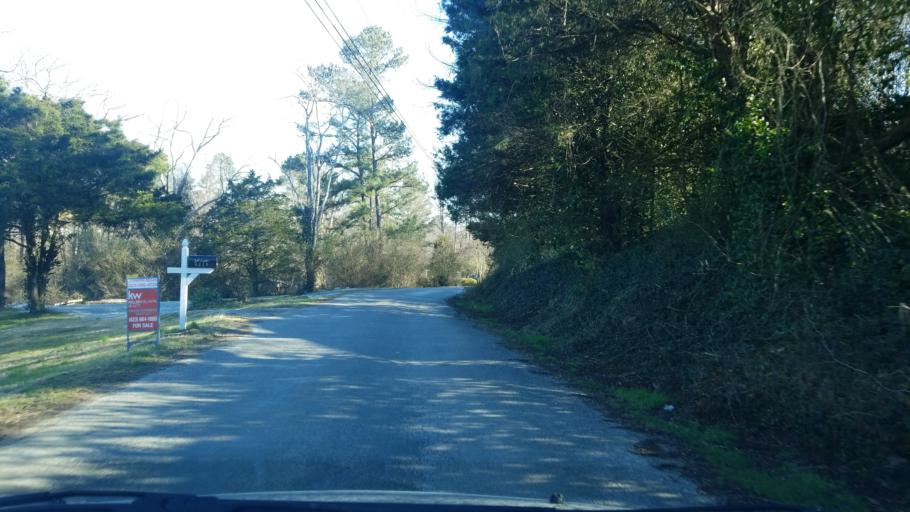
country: US
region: Tennessee
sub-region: Hamilton County
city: Collegedale
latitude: 35.0730
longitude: -85.1007
